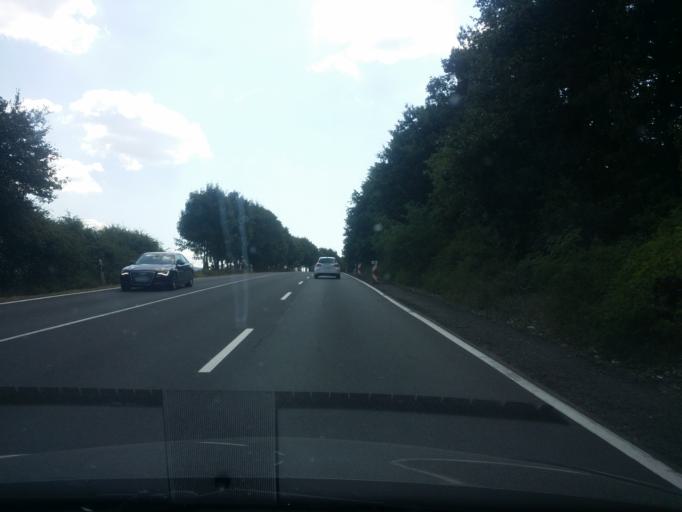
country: HU
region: Nograd
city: Retsag
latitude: 47.8956
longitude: 19.0999
